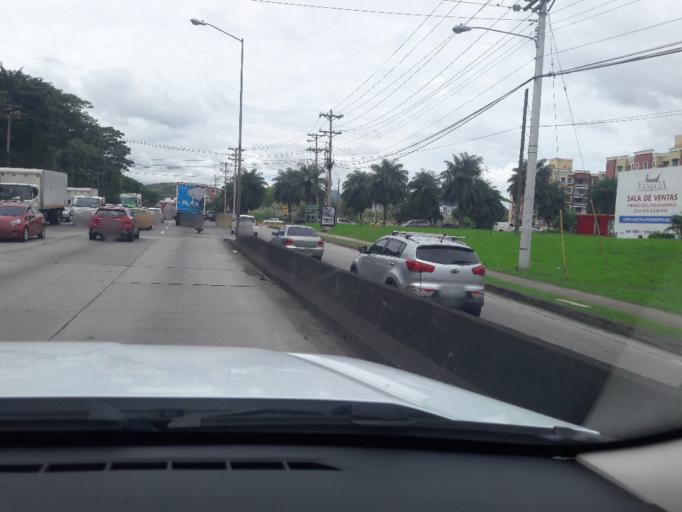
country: PA
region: Panama
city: Panama
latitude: 9.0244
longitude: -79.5277
